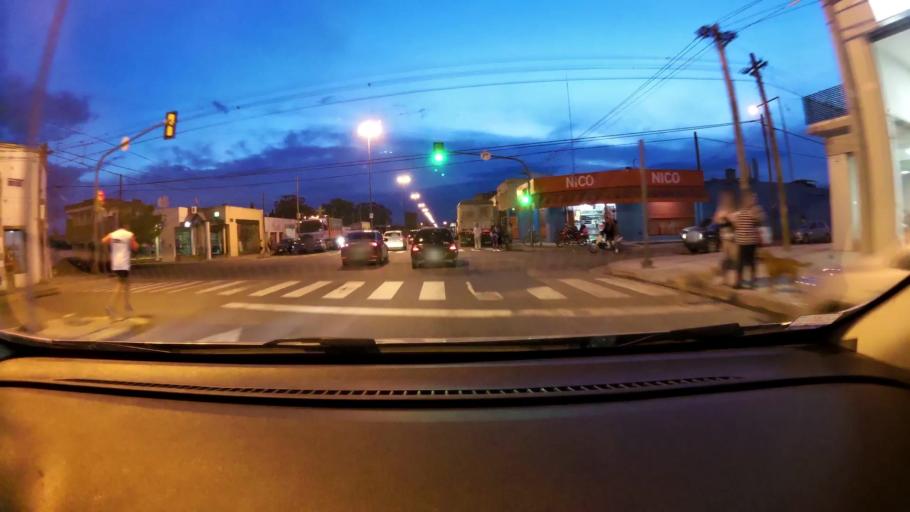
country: AR
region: Buenos Aires
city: San Nicolas de los Arroyos
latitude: -33.3533
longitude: -60.2417
